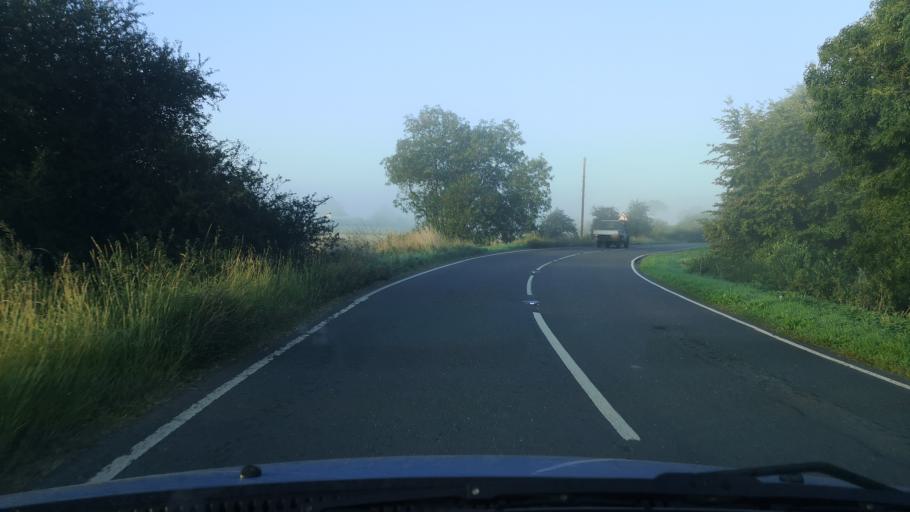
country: GB
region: England
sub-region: North Lincolnshire
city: Eastoft
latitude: 53.6582
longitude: -0.7738
